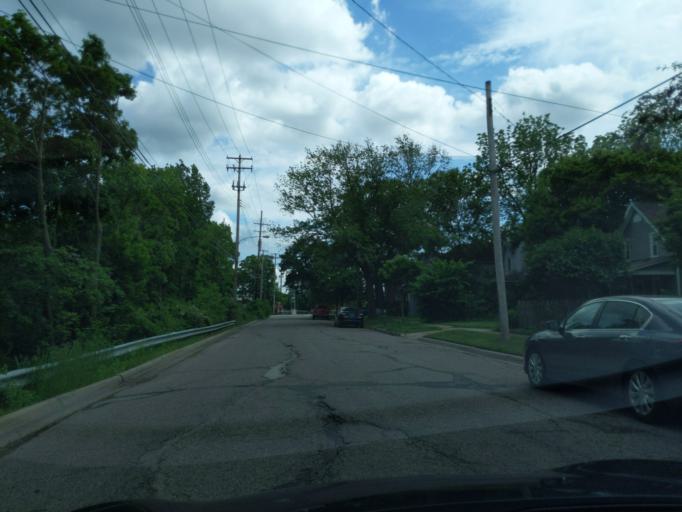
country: US
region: Michigan
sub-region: Ingham County
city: Lansing
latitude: 42.7214
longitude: -84.5494
